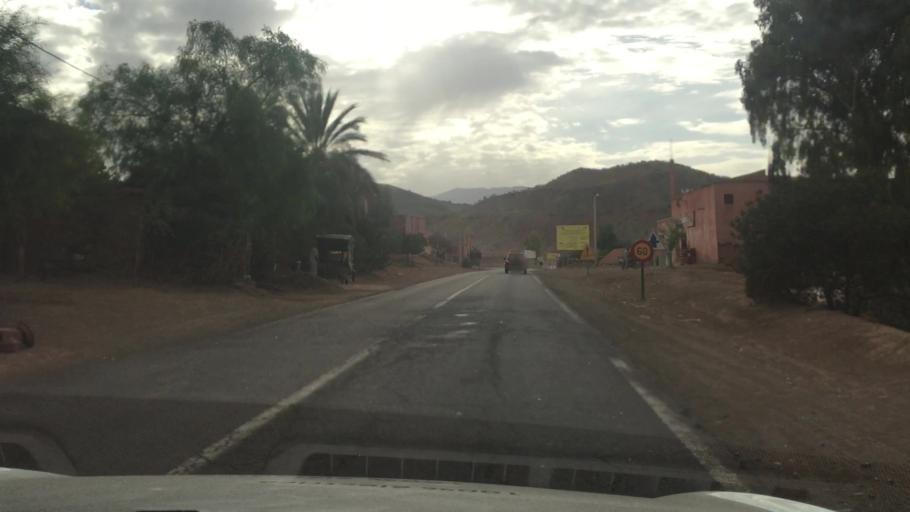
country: MA
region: Marrakech-Tensift-Al Haouz
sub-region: Al-Haouz
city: Touama
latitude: 31.5470
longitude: -7.5739
